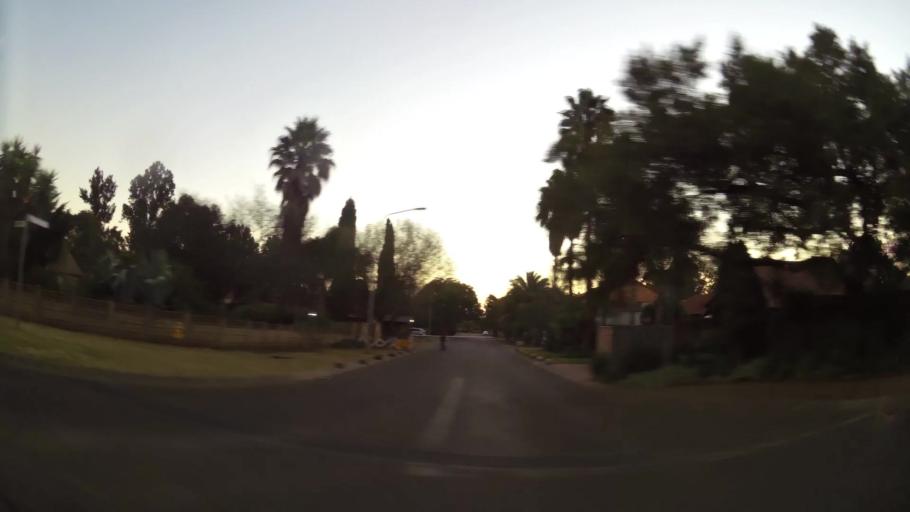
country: ZA
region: Gauteng
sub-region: City of Tshwane Metropolitan Municipality
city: Centurion
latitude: -25.8579
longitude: 28.1343
